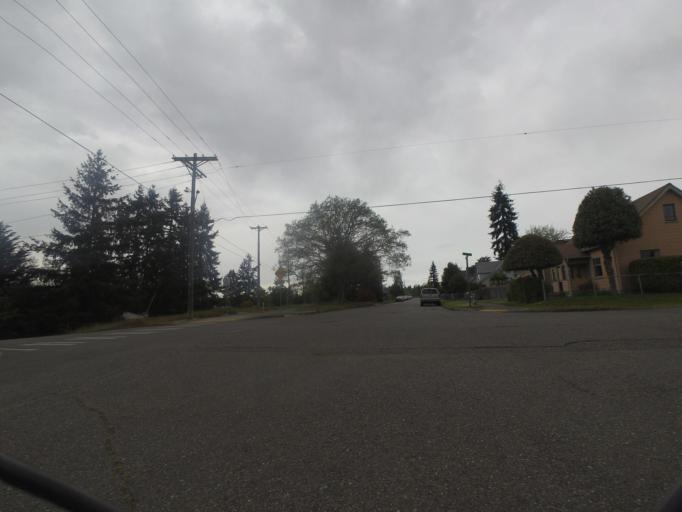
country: US
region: Washington
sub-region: Pierce County
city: Lakewood
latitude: 47.2009
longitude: -122.4756
